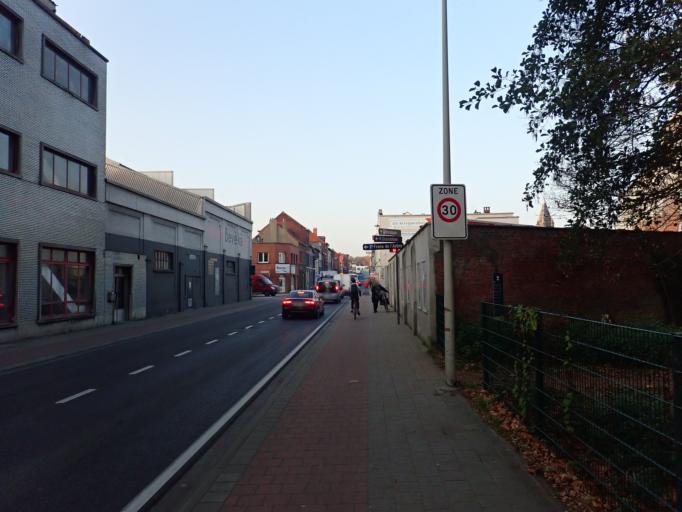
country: BE
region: Flanders
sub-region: Provincie Antwerpen
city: Antwerpen
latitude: 51.2434
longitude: 4.4500
